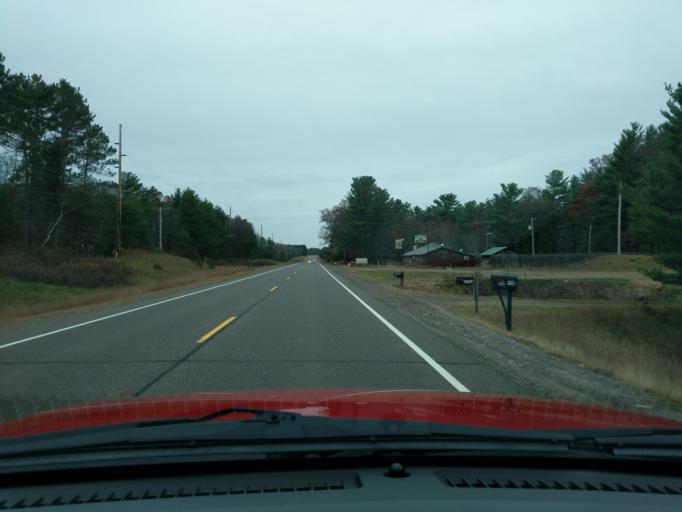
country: US
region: Wisconsin
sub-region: Burnett County
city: Siren
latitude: 45.8107
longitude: -92.2237
